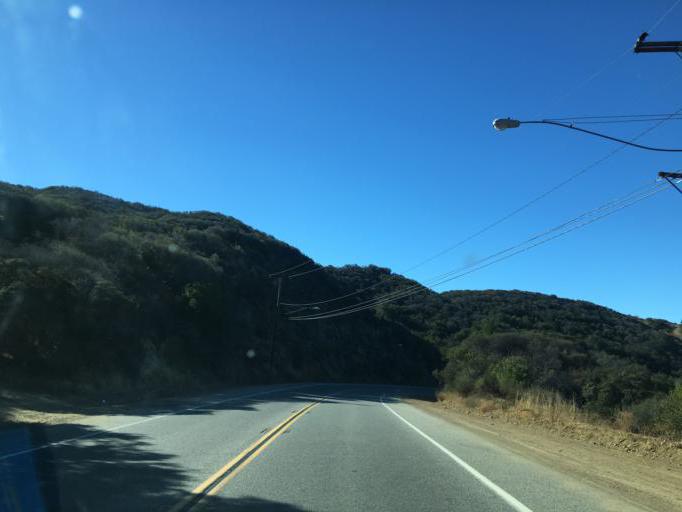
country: US
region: California
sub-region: Los Angeles County
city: Westlake Village
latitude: 34.0865
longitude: -118.8164
